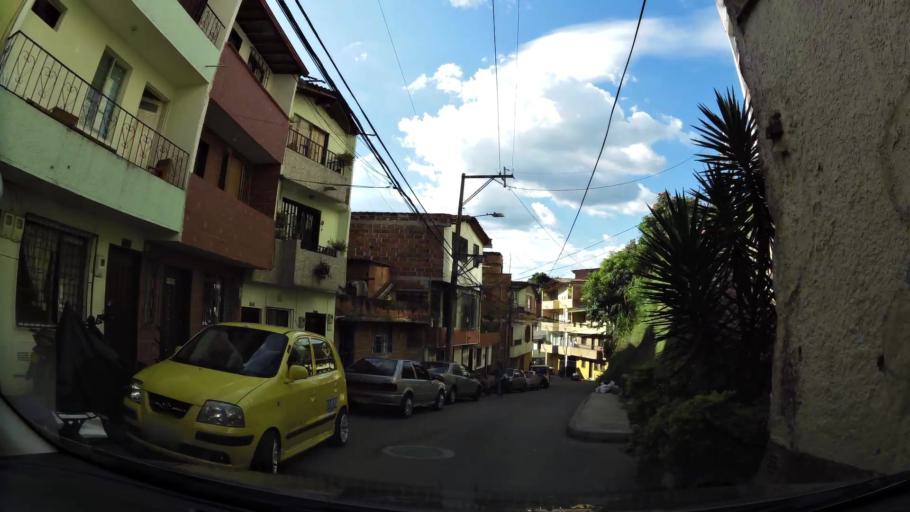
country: CO
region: Antioquia
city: Envigado
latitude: 6.1763
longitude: -75.5786
